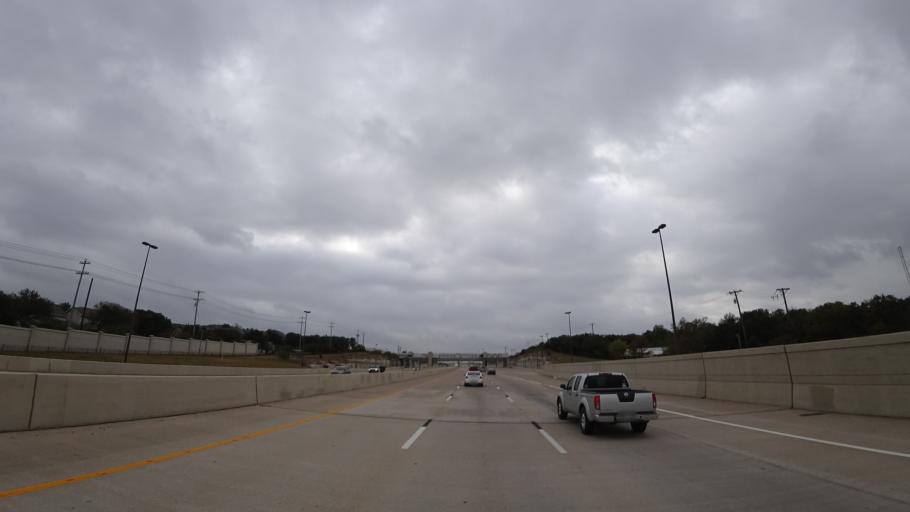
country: US
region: Texas
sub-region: Williamson County
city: Cedar Park
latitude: 30.5171
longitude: -97.8144
